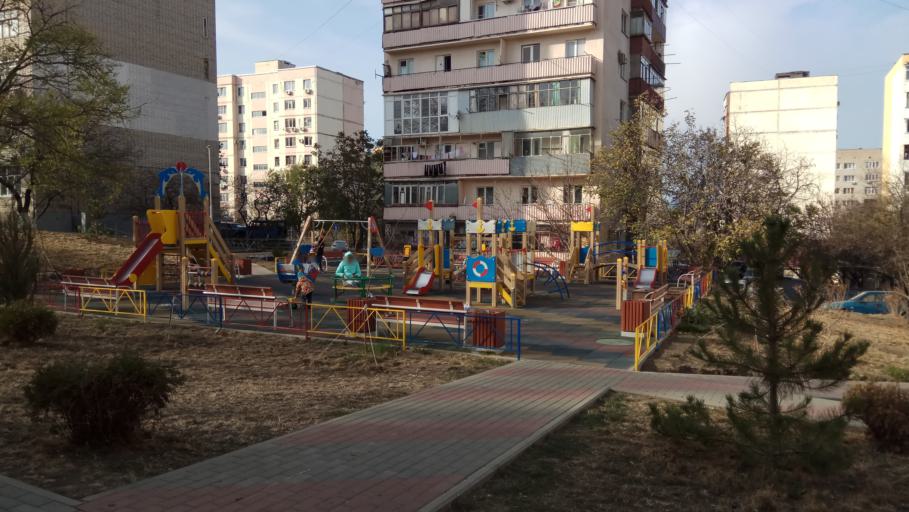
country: RU
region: Krasnodarskiy
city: Gelendzhik
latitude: 44.5472
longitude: 38.0795
